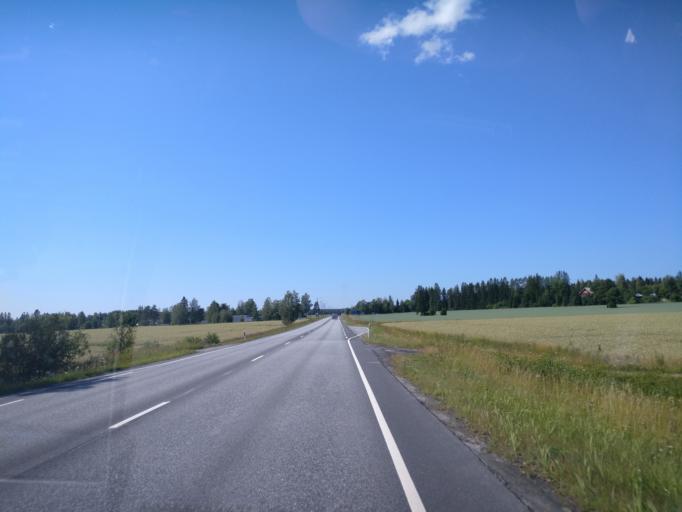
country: FI
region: Satakunta
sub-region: Pori
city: Nakkila
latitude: 61.4590
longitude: 22.0208
